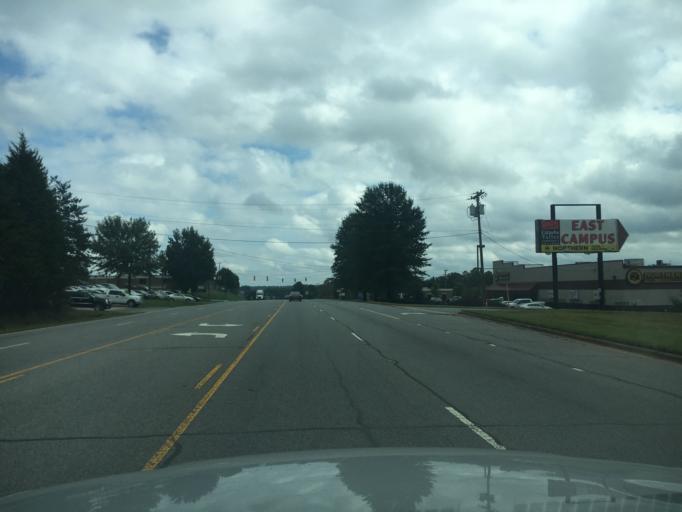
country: US
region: North Carolina
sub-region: Catawba County
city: Conover
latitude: 35.6993
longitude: -81.2819
